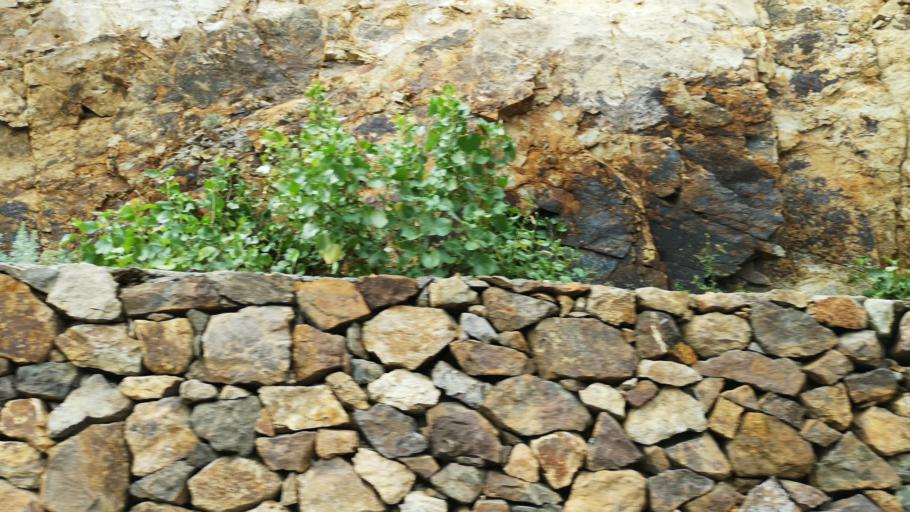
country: ES
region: Canary Islands
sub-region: Provincia de Santa Cruz de Tenerife
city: Vallehermosa
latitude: 28.1757
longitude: -17.2702
